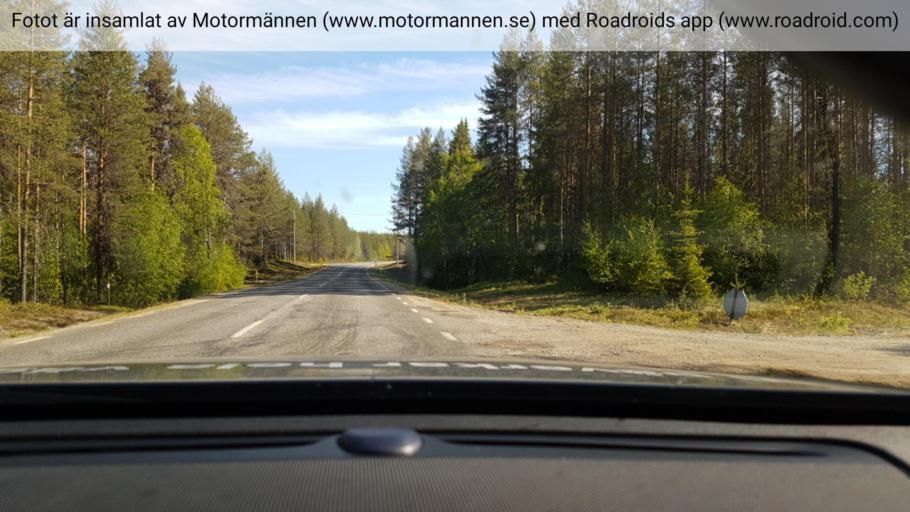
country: SE
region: Vaesterbotten
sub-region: Norsjo Kommun
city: Norsjoe
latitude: 64.7311
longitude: 19.1311
